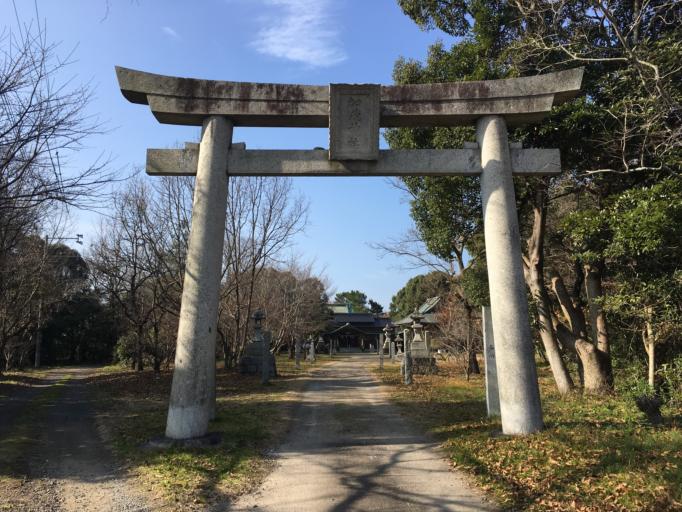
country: JP
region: Fukuoka
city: Nakatsu
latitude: 33.5990
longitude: 131.2361
